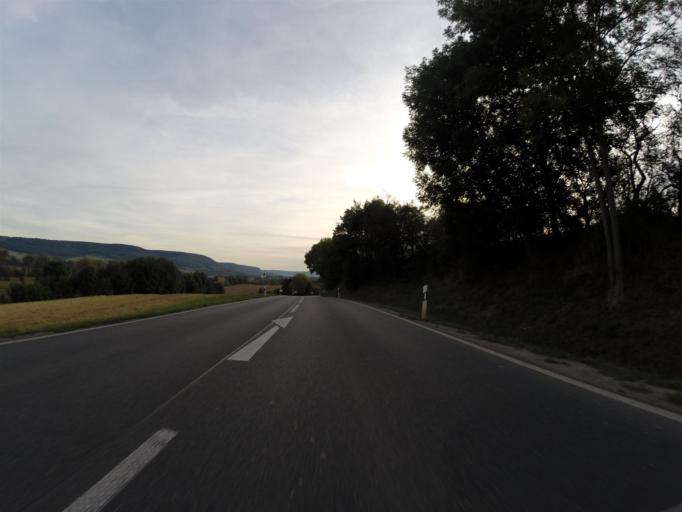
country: DE
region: Thuringia
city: Neuengonna
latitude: 50.9709
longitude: 11.6325
